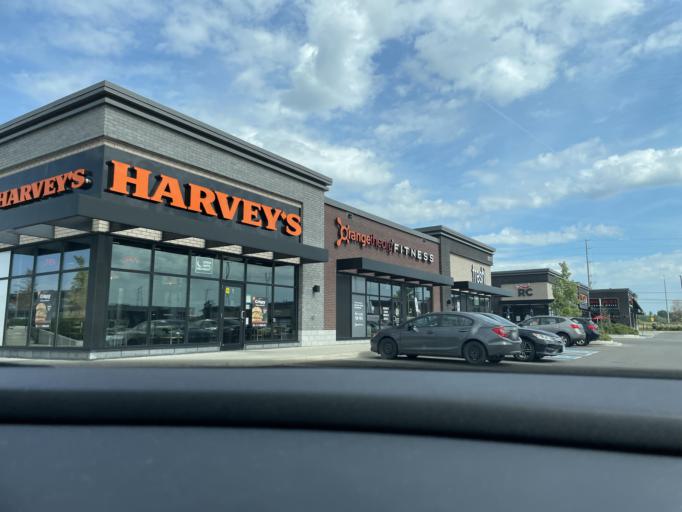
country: CA
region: Ontario
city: Brampton
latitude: 43.6350
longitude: -79.7890
